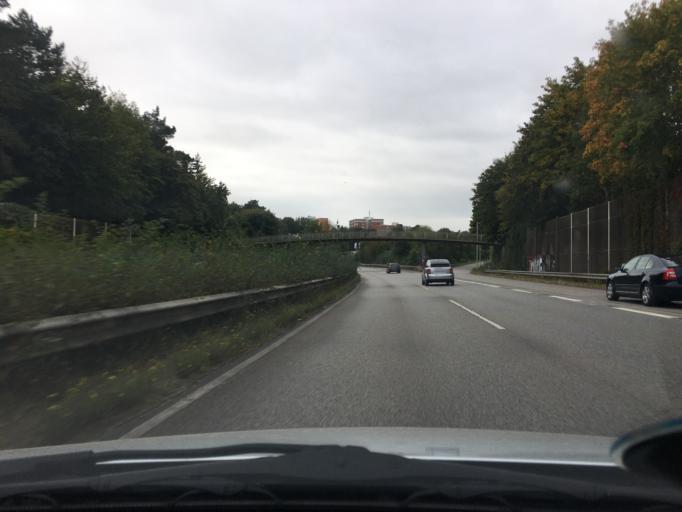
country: DE
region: Schleswig-Holstein
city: Kiel
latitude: 54.3600
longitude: 10.1207
